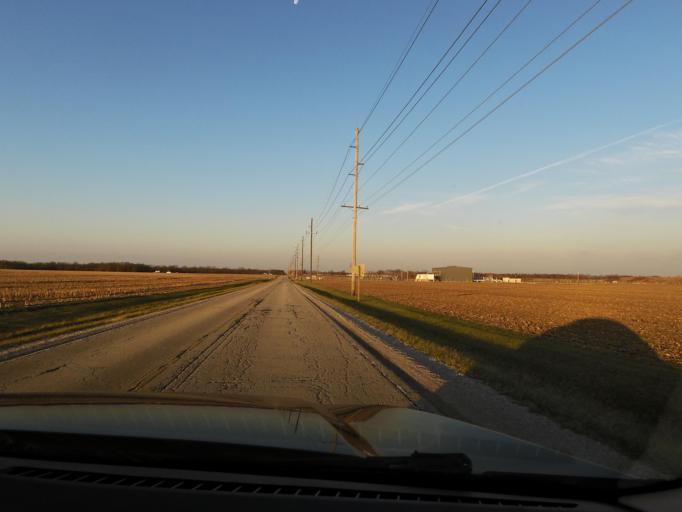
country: US
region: Illinois
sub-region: Marion County
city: Odin
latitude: 38.7650
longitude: -89.0368
